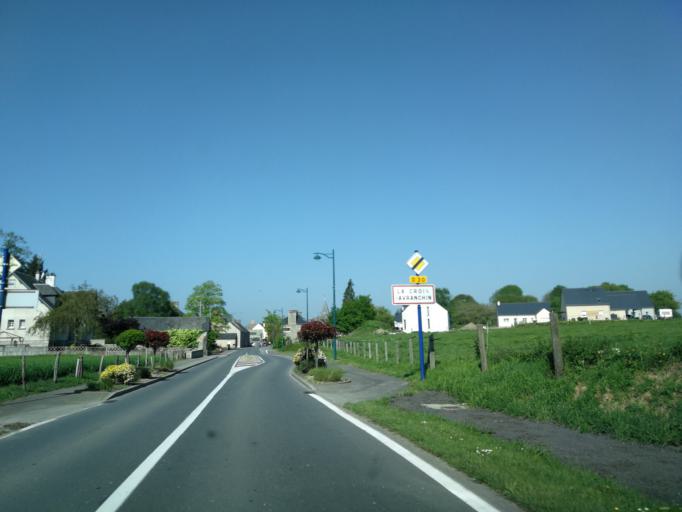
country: FR
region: Lower Normandy
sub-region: Departement de la Manche
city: Saint-James
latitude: 48.5451
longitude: -1.3782
